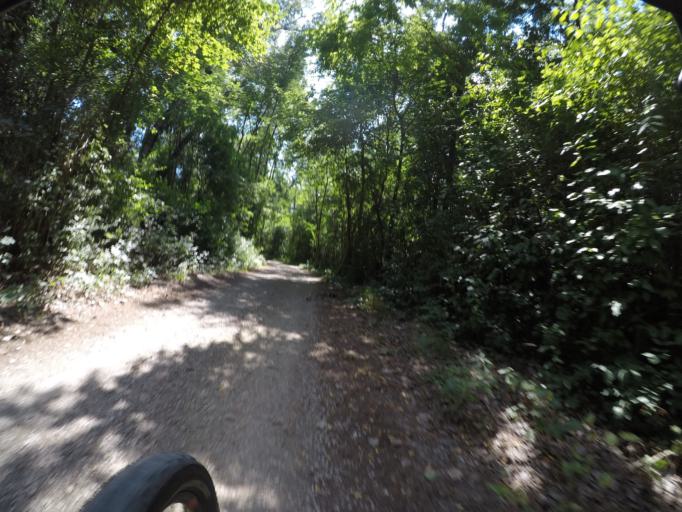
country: AT
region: Lower Austria
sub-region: Politischer Bezirk Ganserndorf
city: Gross-Enzersdorf
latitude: 48.1851
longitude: 16.5355
